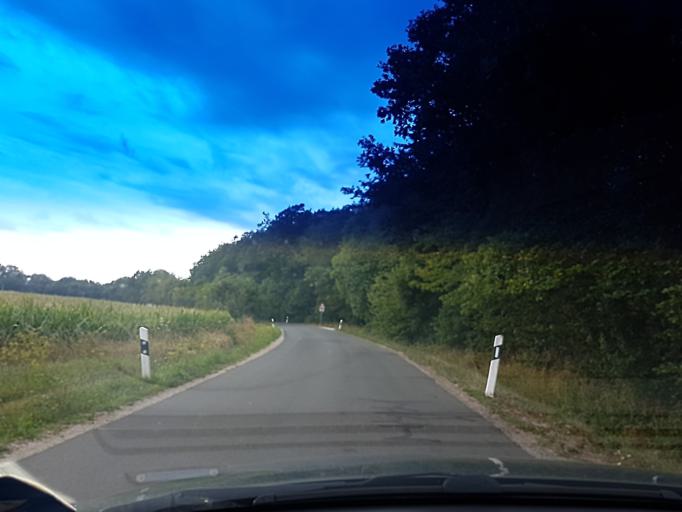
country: DE
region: Bavaria
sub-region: Upper Franconia
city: Frensdorf
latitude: 49.8346
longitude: 10.8701
